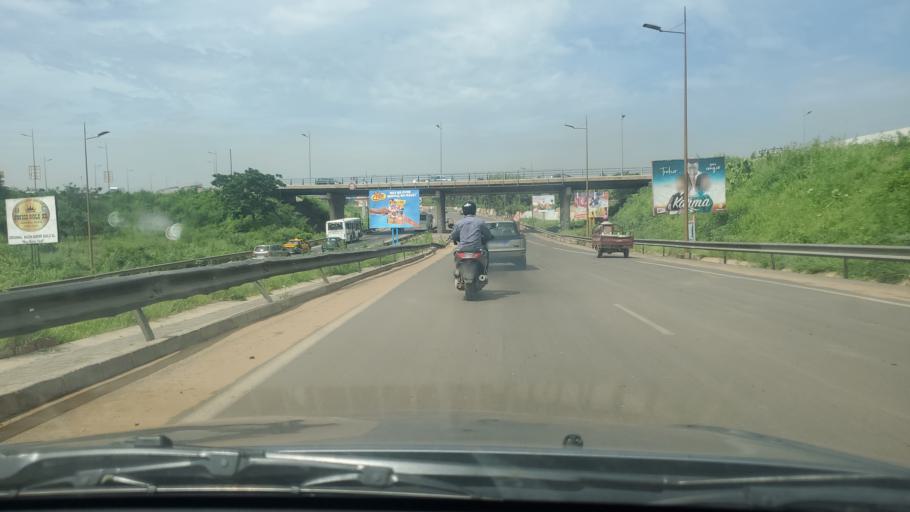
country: SN
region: Dakar
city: Grand Dakar
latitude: 14.7422
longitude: -17.4367
